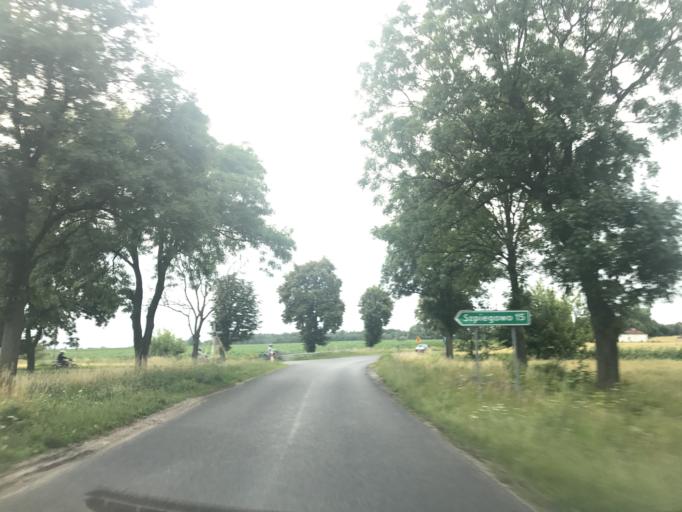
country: PL
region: Kujawsko-Pomorskie
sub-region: Powiat lipnowski
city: Lipno
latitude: 52.8095
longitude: 19.1854
